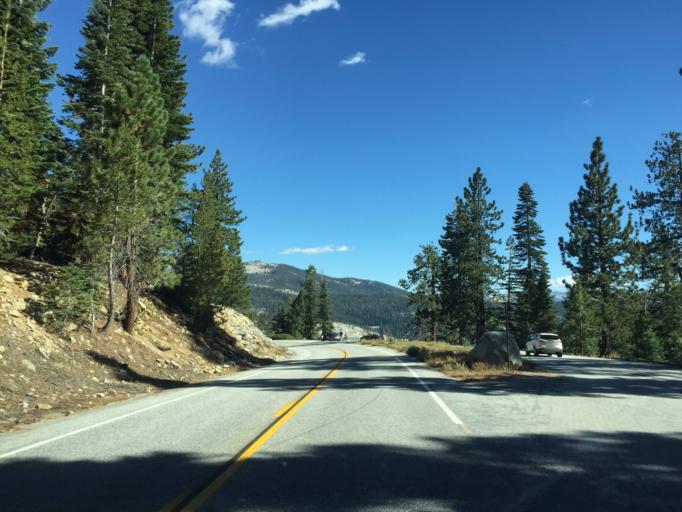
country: US
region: California
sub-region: Mariposa County
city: Yosemite Valley
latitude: 37.8492
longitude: -119.6124
